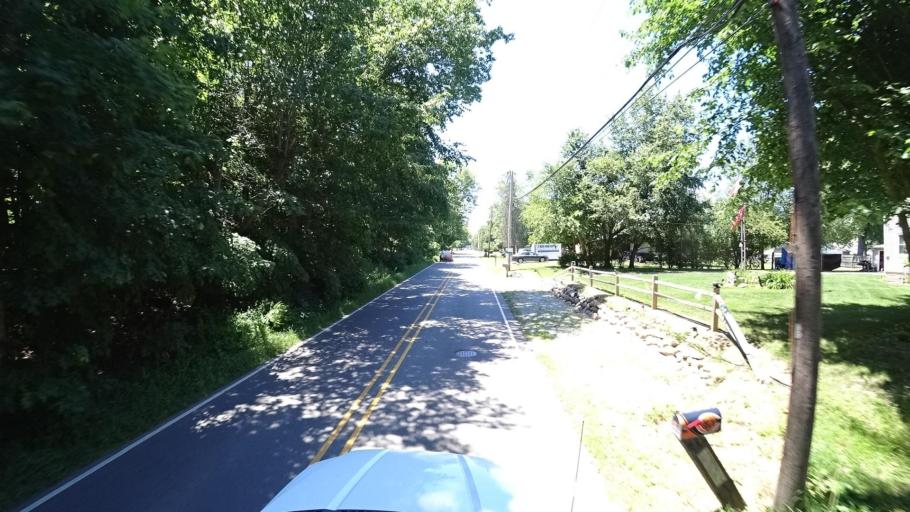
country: US
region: Indiana
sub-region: Porter County
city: Chesterton
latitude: 41.6168
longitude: -87.0524
